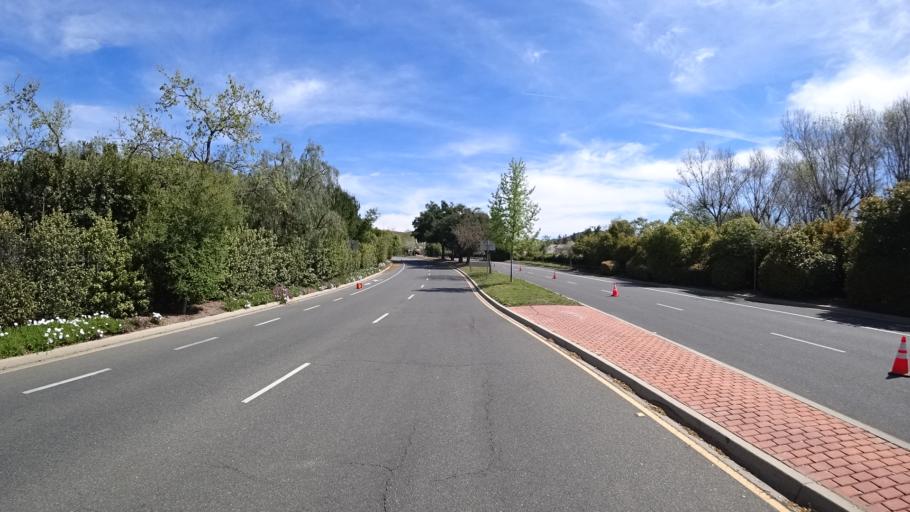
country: US
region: California
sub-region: Ventura County
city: Thousand Oaks
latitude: 34.1970
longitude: -118.8223
